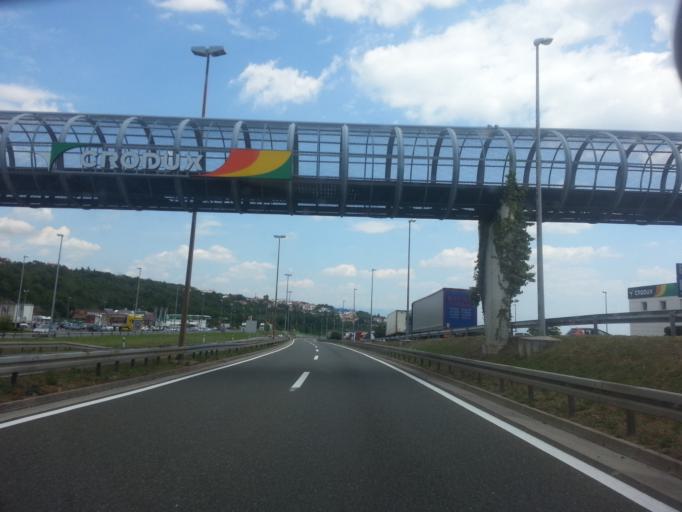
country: HR
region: Primorsko-Goranska
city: Rubesi
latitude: 45.3555
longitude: 14.3498
